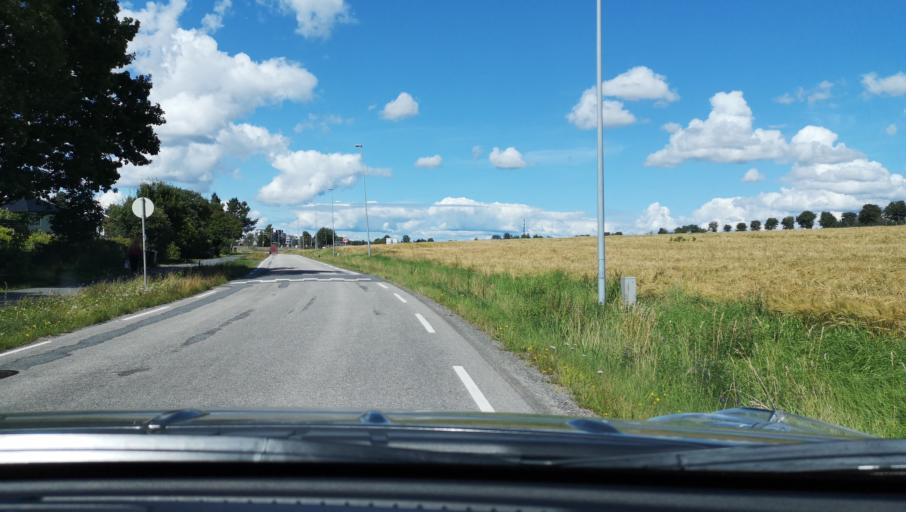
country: NO
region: Akershus
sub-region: As
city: As
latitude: 59.6567
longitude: 10.7993
